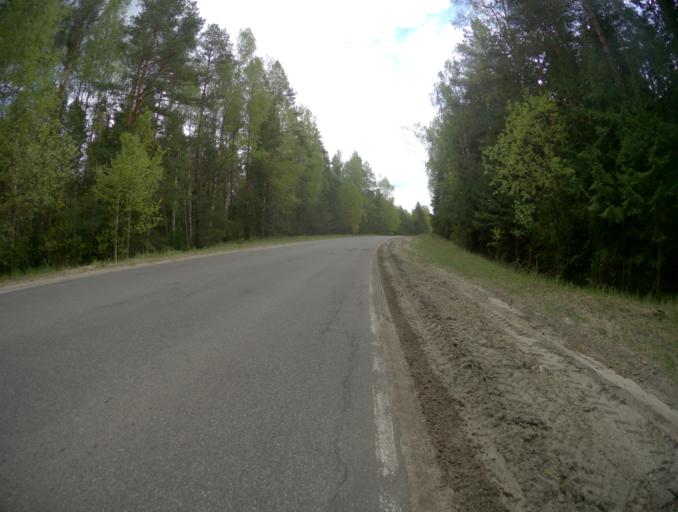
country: RU
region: Vladimir
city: Velikodvorskiy
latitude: 55.3946
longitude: 40.7182
